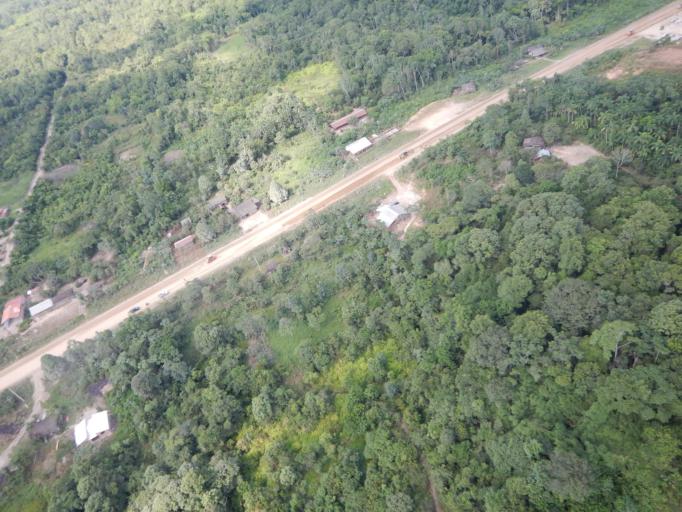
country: BO
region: Cochabamba
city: Chimore
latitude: -16.8244
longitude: -65.5440
